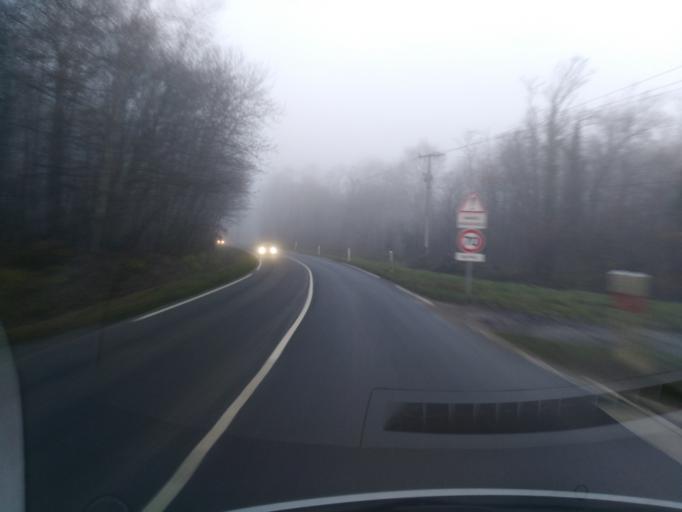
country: FR
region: Ile-de-France
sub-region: Departement des Yvelines
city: Orgeval
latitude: 48.9179
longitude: 1.9569
